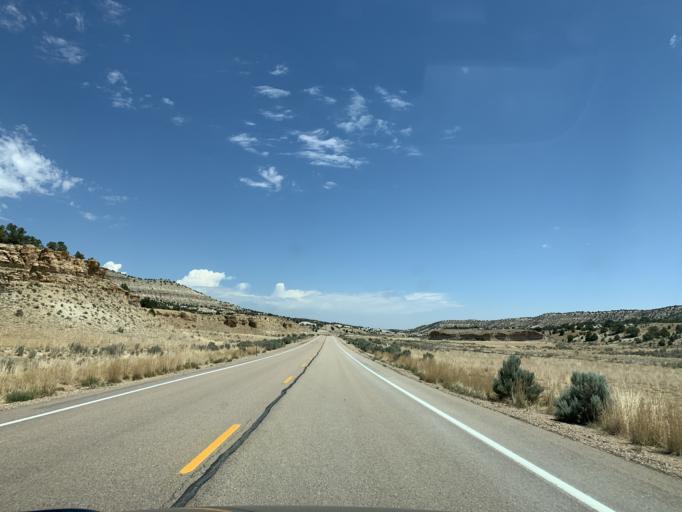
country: US
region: Utah
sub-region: Duchesne County
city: Duchesne
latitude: 39.9412
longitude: -110.2111
